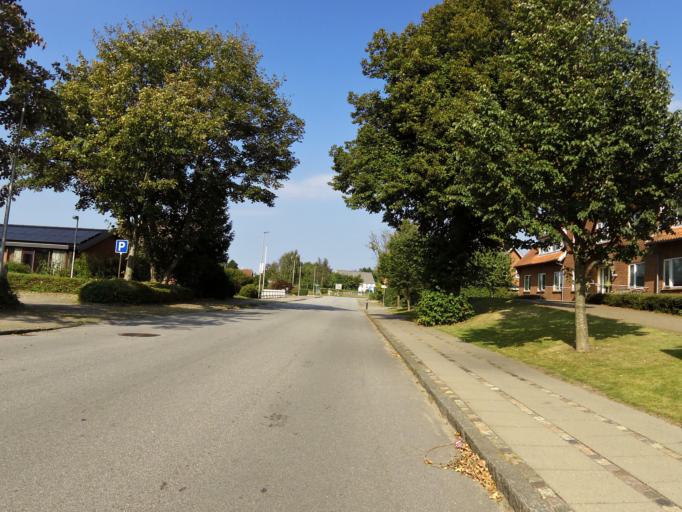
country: DK
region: South Denmark
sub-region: Vejen Kommune
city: Vejen
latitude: 55.4209
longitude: 9.1532
